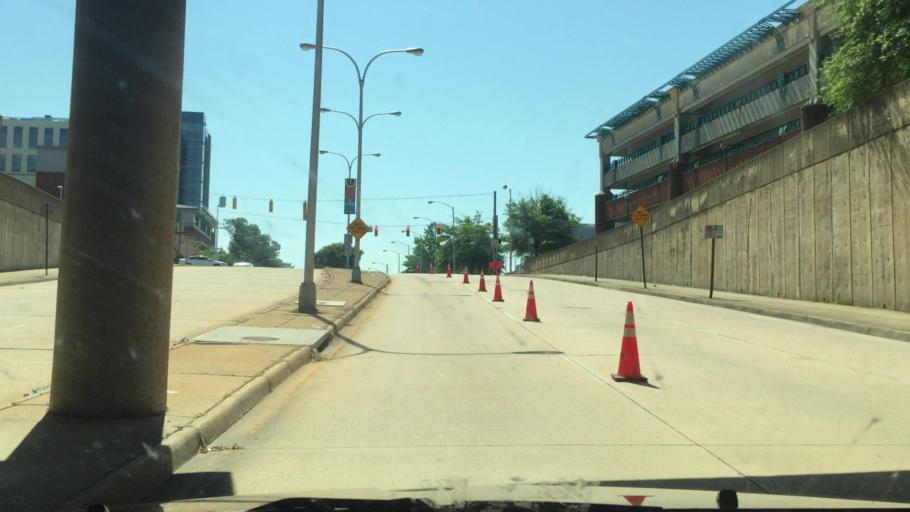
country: US
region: Virginia
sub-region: City of Richmond
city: Richmond
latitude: 37.5447
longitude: -77.4329
